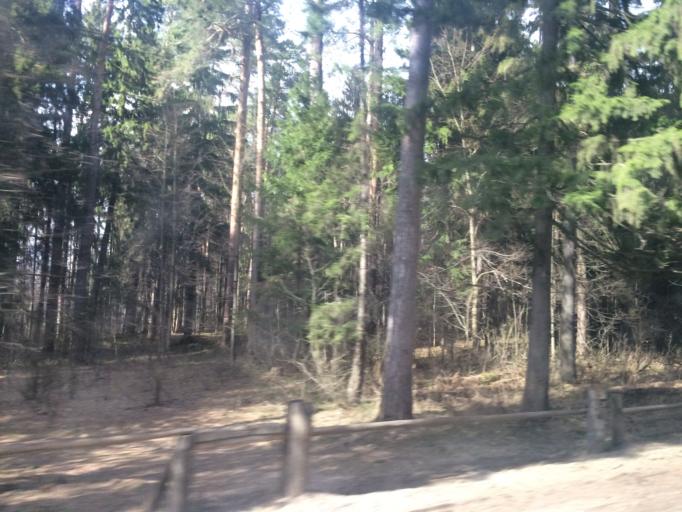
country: RU
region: Tatarstan
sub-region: Zelenodol'skiy Rayon
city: Vasil'yevo
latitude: 55.8964
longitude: 48.7306
